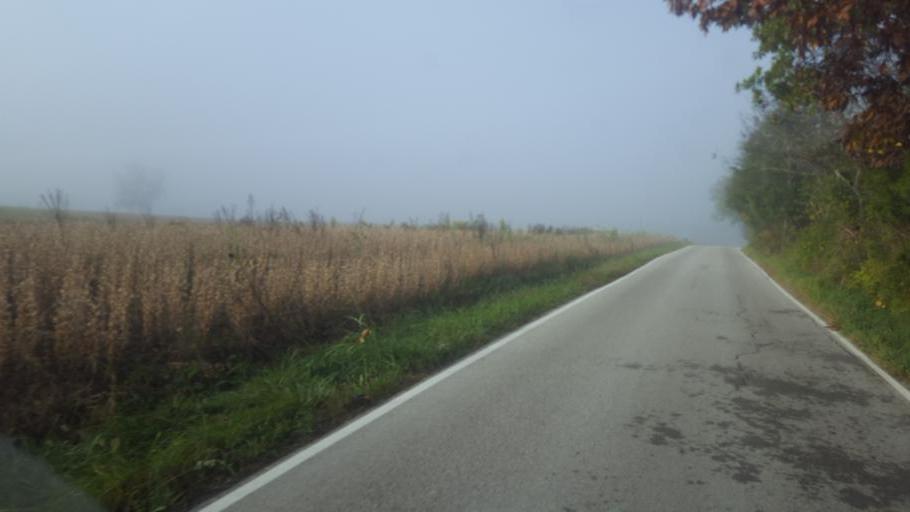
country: US
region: Kentucky
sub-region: Fleming County
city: Flemingsburg
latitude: 38.4933
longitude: -83.5806
